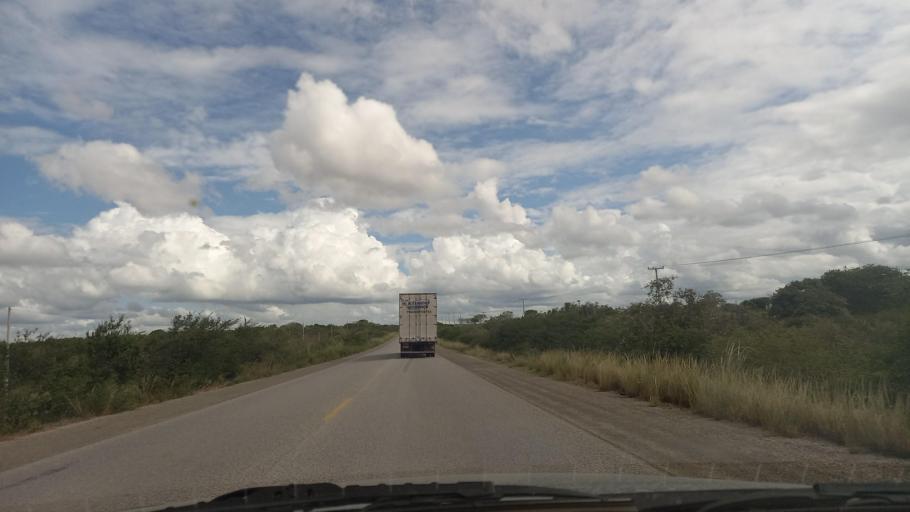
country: BR
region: Pernambuco
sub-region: Cachoeirinha
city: Cachoeirinha
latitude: -8.4126
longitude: -36.1900
